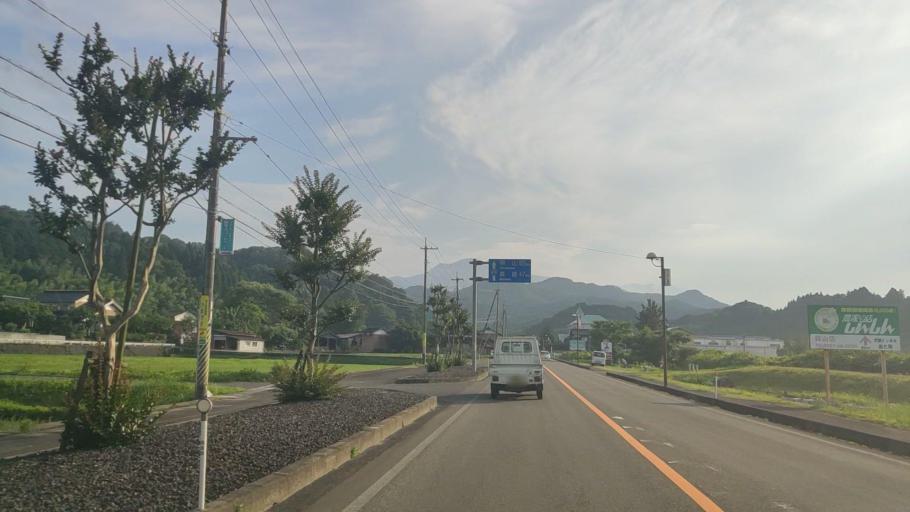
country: JP
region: Tottori
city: Kurayoshi
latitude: 35.3642
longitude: 133.7565
